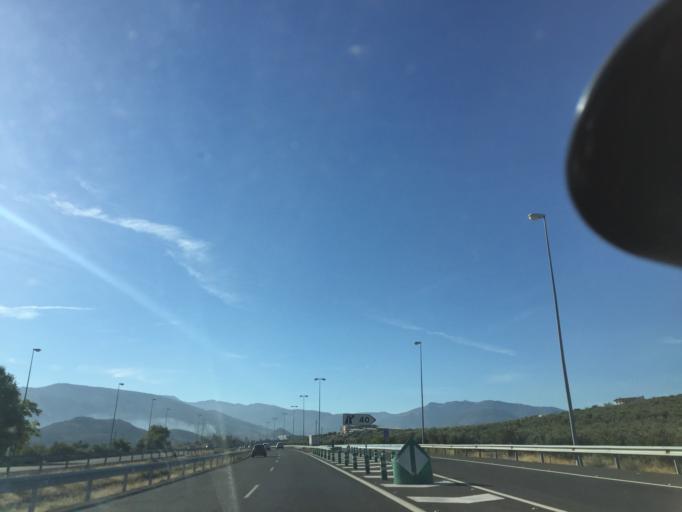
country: ES
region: Andalusia
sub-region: Provincia de Jaen
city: Jaen
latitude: 37.7906
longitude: -3.7580
